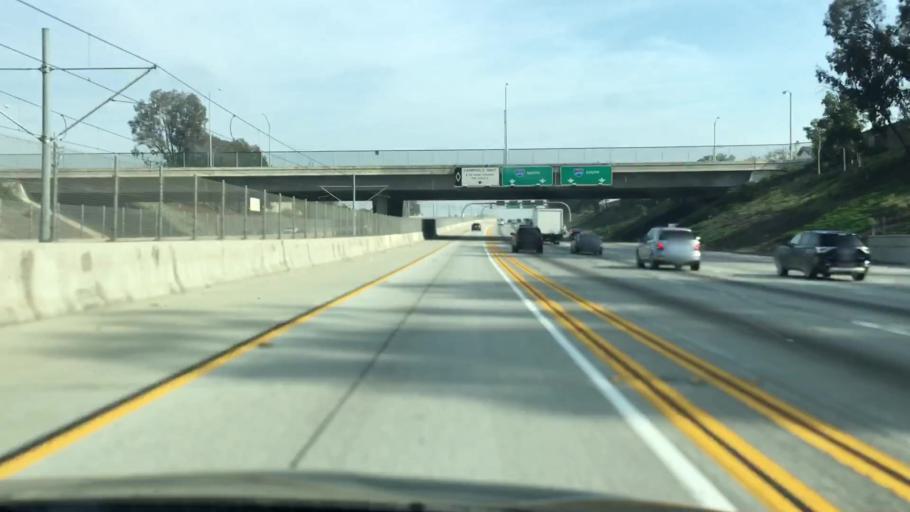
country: US
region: California
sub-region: Los Angeles County
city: Downey
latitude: 33.9137
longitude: -118.1180
